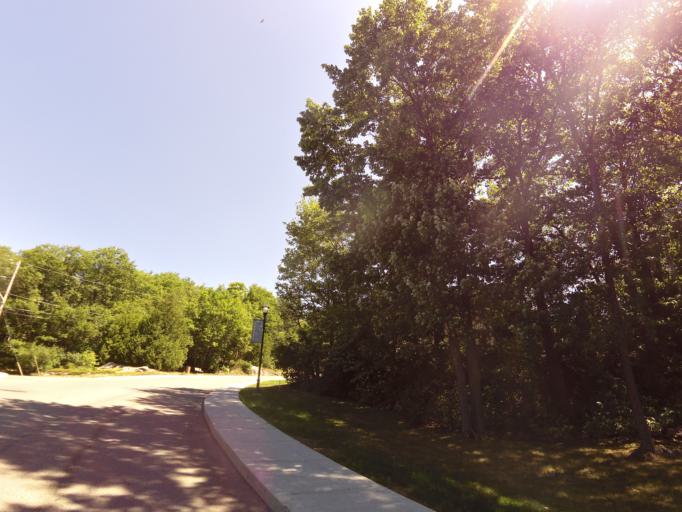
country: CA
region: Quebec
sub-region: Abitibi-Temiscamingue
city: Temiscaming
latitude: 46.7180
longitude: -79.1027
